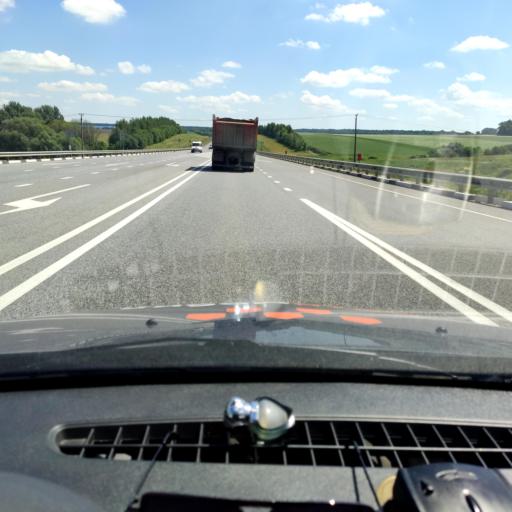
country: RU
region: Orjol
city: Zmiyevka
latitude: 52.8275
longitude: 36.2726
